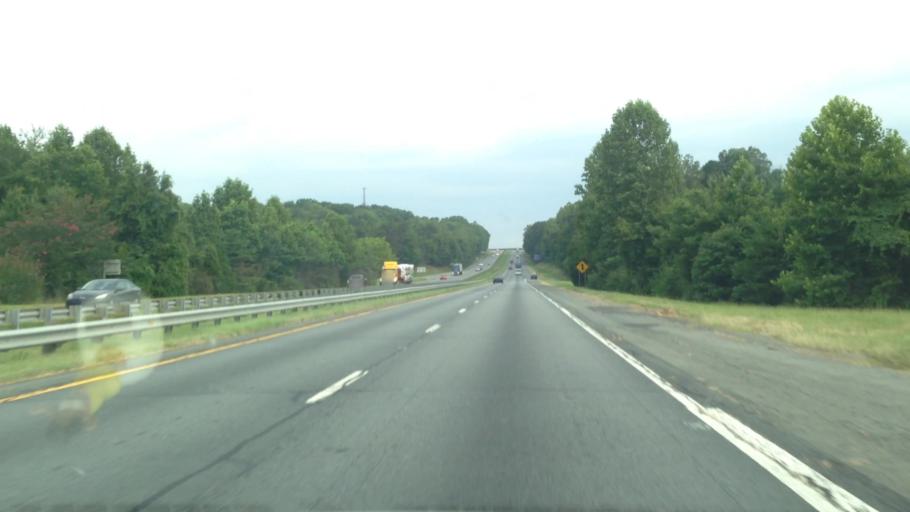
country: US
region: North Carolina
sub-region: Forsyth County
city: Tobaccoville
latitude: 36.2487
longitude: -80.3531
